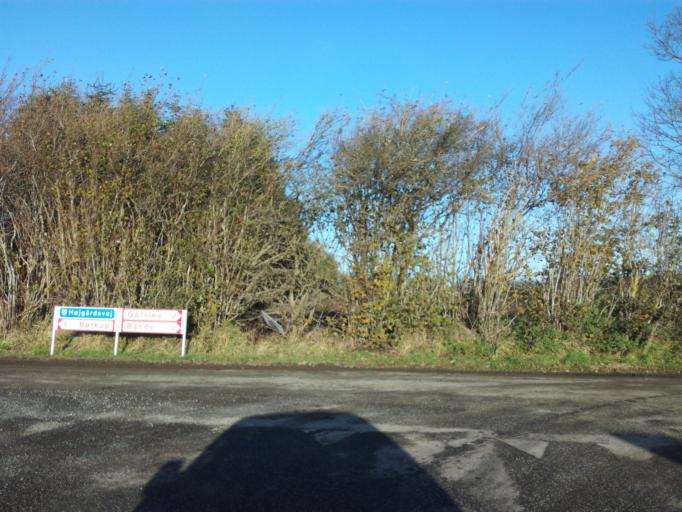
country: DK
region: South Denmark
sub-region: Vejle Kommune
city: Borkop
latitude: 55.6294
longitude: 9.6776
